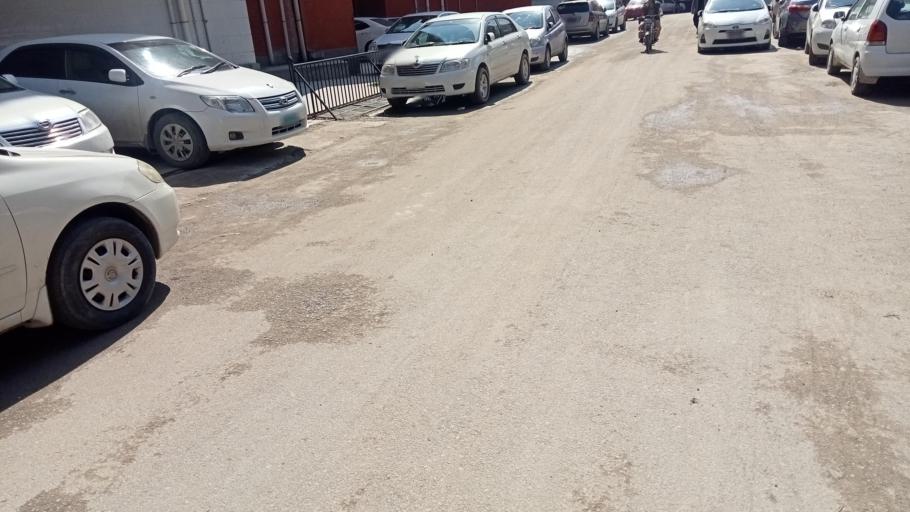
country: PK
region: Khyber Pakhtunkhwa
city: Saidu Sharif
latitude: 34.7496
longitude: 72.3551
